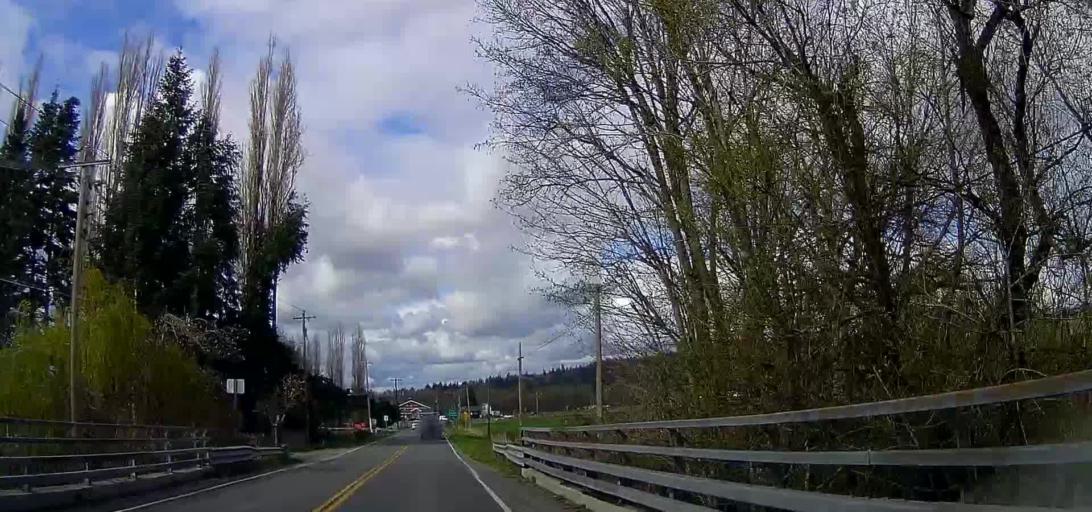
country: US
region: Washington
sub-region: Snohomish County
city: Smokey Point
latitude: 48.1848
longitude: -122.1937
